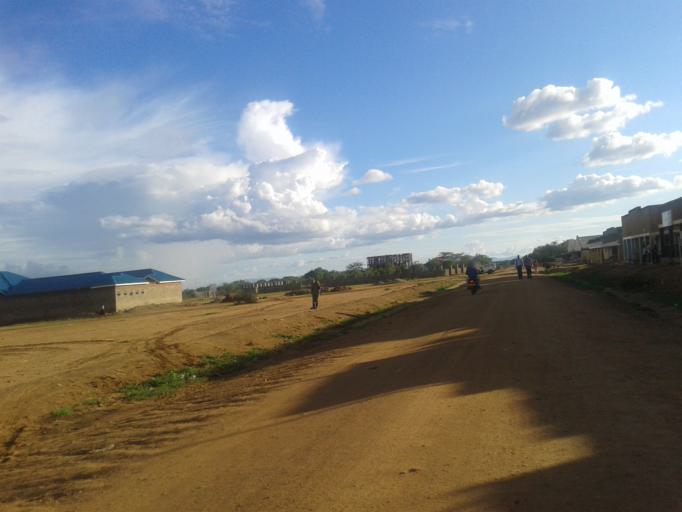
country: UG
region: Northern Region
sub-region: Kotido District
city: Kotido
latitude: 3.0041
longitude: 34.1129
